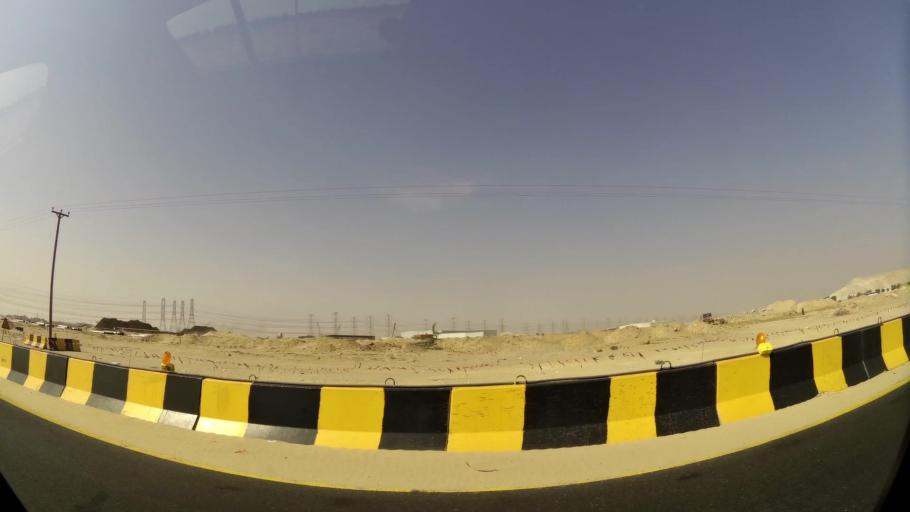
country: KW
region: Al Ahmadi
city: Al Fahahil
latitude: 28.9701
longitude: 48.1279
